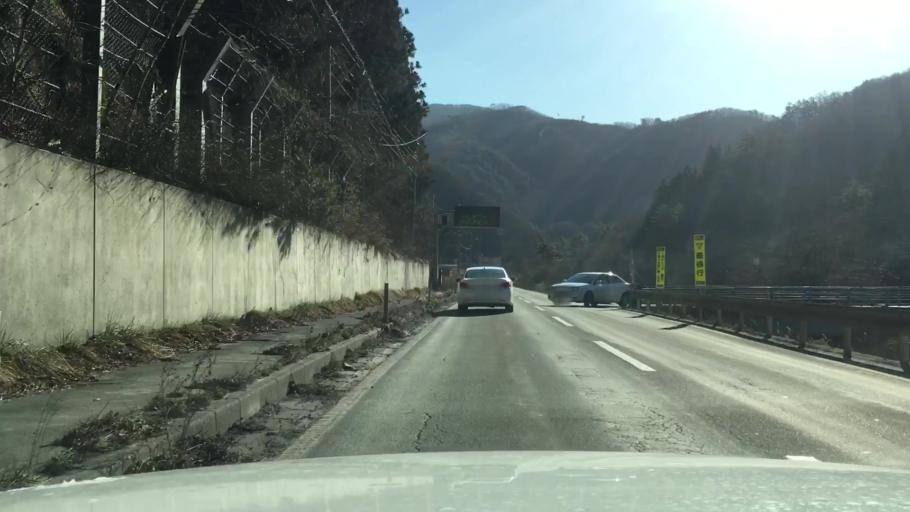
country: JP
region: Iwate
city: Miyako
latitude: 39.5957
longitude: 141.6593
